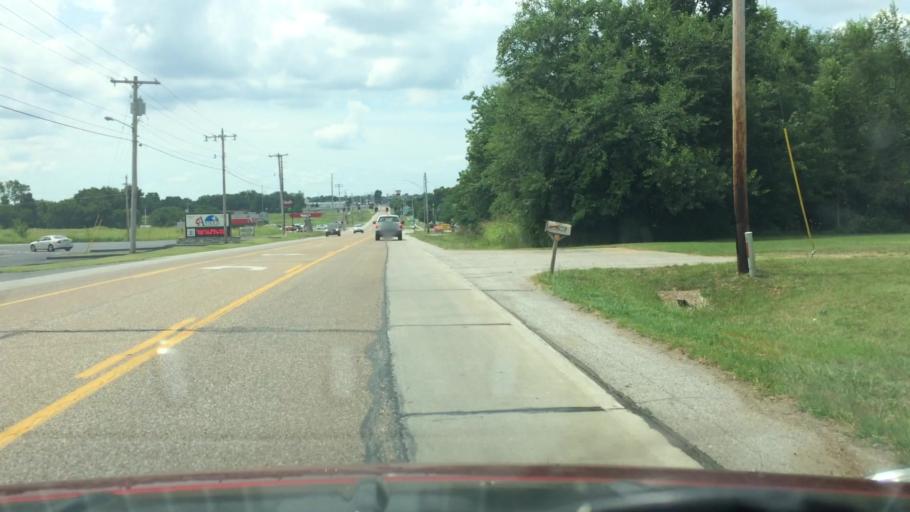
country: US
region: Missouri
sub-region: Greene County
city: Springfield
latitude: 37.2644
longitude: -93.2648
